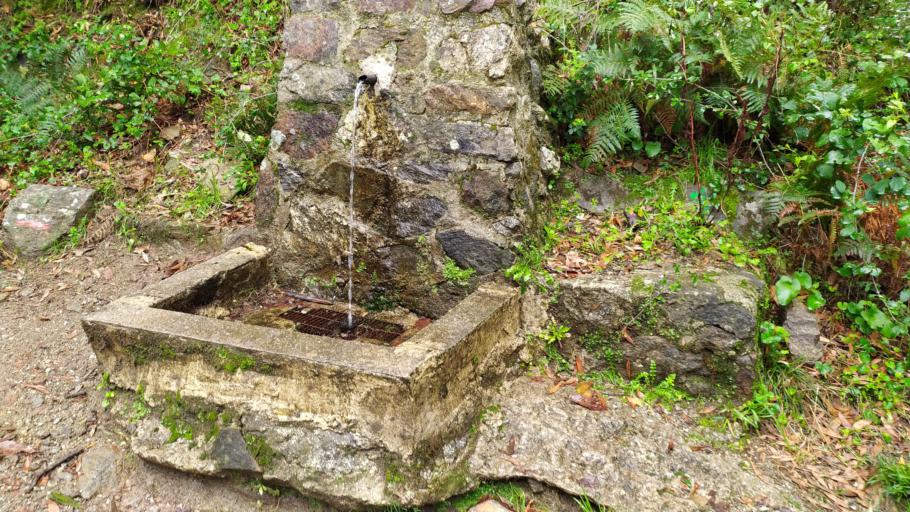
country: IT
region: Sicily
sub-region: Messina
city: Saponara
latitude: 38.2065
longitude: 15.4902
